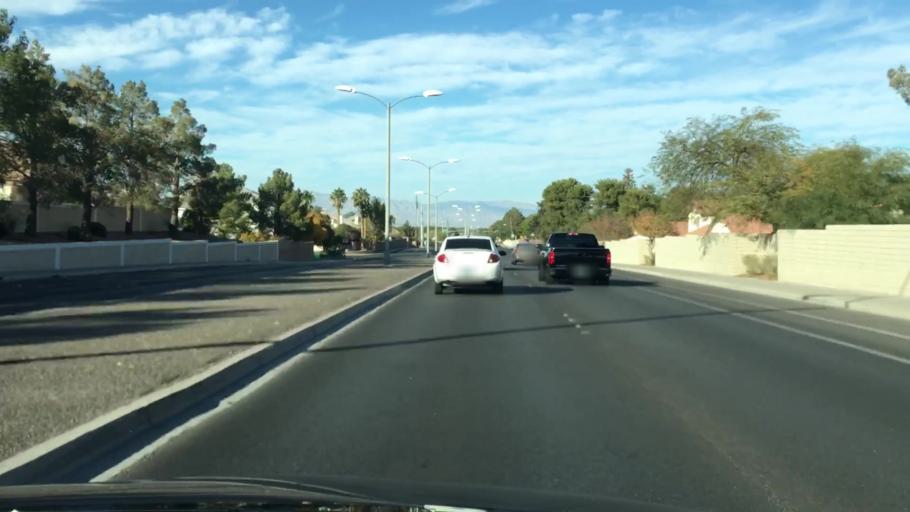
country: US
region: Nevada
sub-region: Clark County
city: Whitney
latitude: 36.0526
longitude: -115.1003
